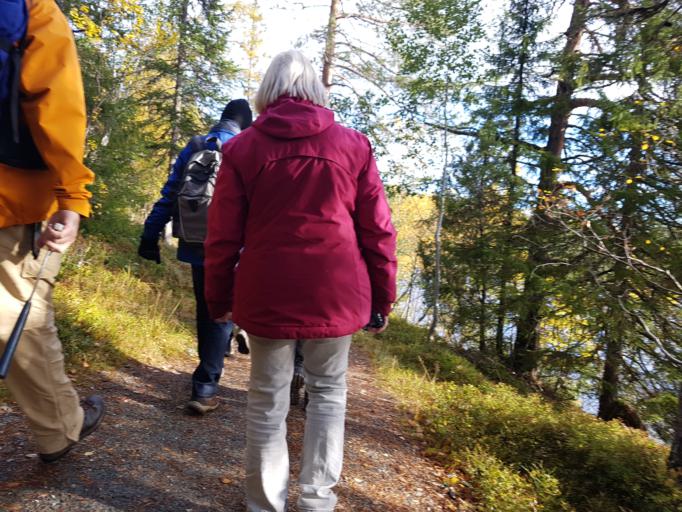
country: NO
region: Sor-Trondelag
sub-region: Trondheim
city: Trondheim
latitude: 63.4246
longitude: 10.2781
